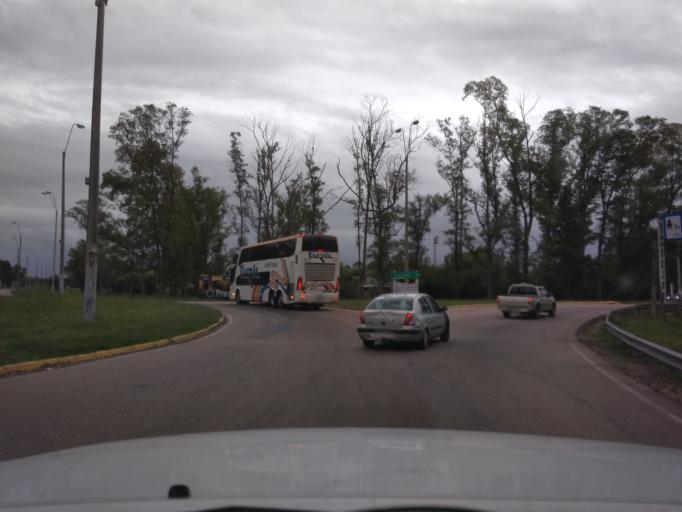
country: UY
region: Canelones
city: Canelones
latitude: -34.5222
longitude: -56.2711
